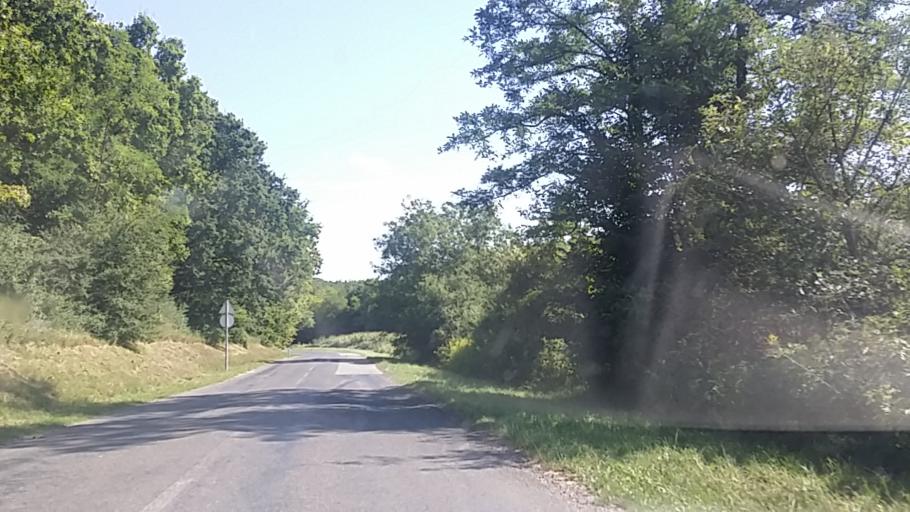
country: HU
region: Tolna
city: Gyonk
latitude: 46.5386
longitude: 18.4589
